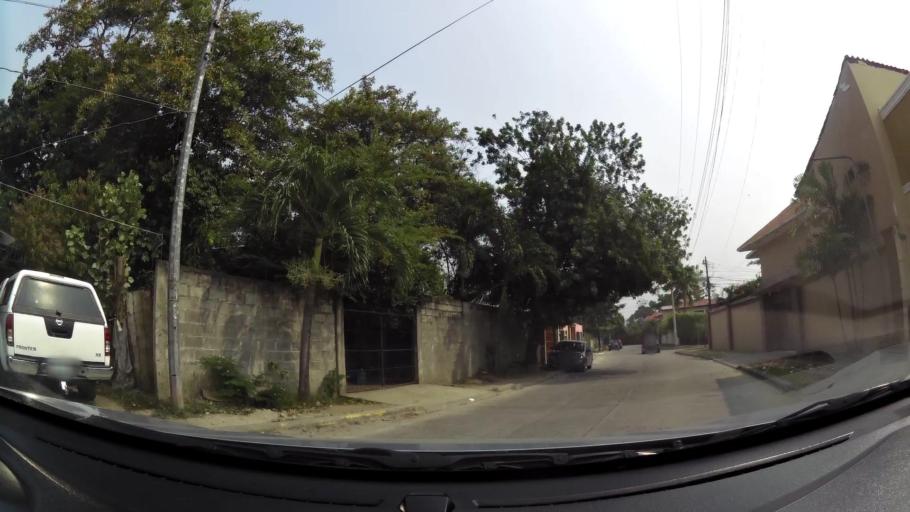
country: HN
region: Cortes
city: El Zapotal del Norte
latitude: 15.5249
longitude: -88.0314
